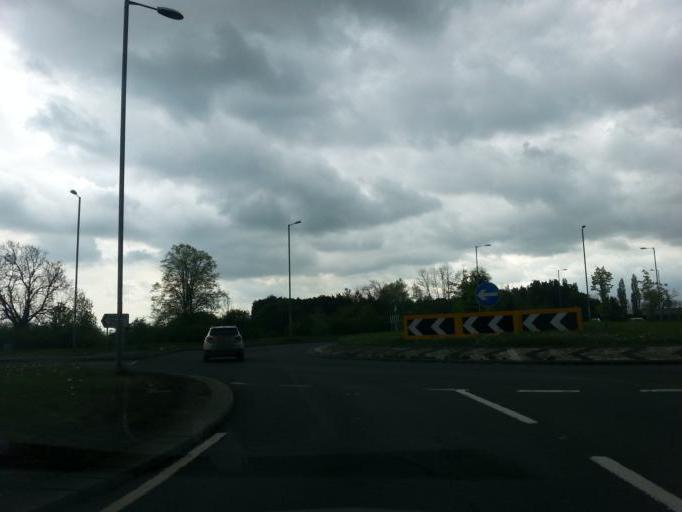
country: GB
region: England
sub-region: Peterborough
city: Thorney
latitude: 52.6210
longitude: -0.1207
